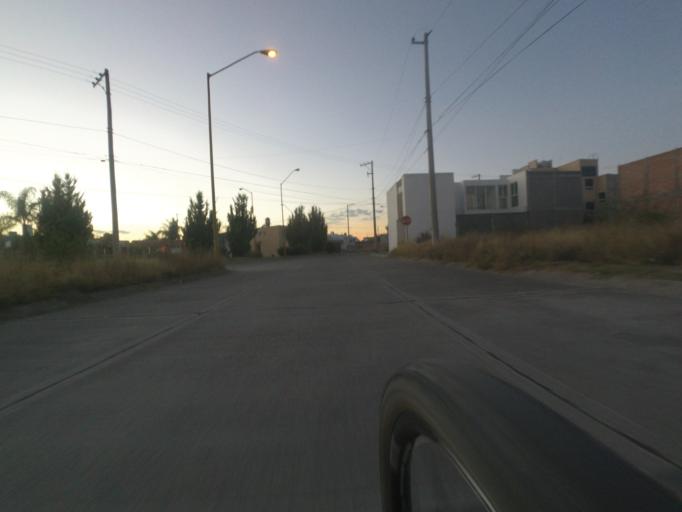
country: MX
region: Aguascalientes
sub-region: Aguascalientes
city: La Loma de los Negritos
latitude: 21.8497
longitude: -102.3314
